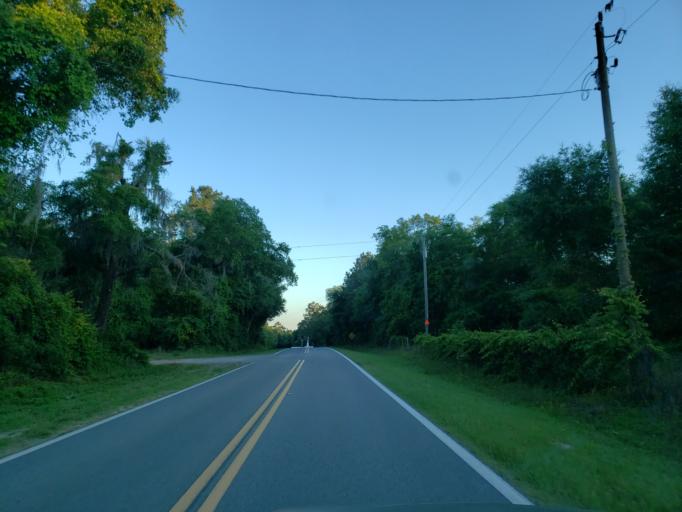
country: US
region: Georgia
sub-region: Lowndes County
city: Valdosta
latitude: 30.6209
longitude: -83.2562
